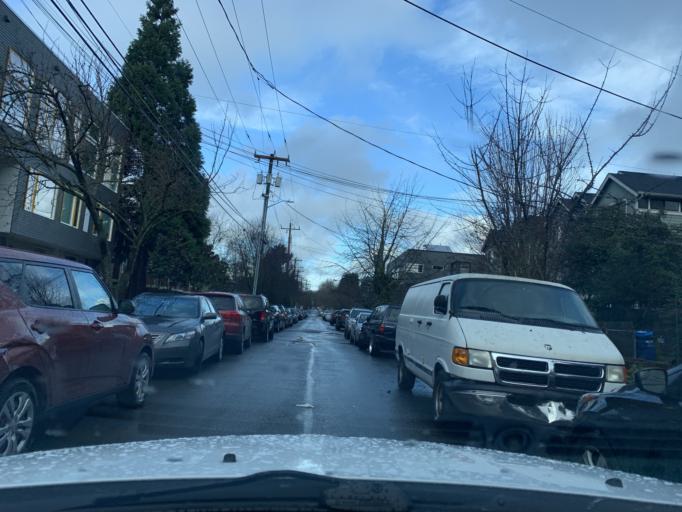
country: US
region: Washington
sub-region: King County
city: Seattle
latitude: 47.6196
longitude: -122.3053
